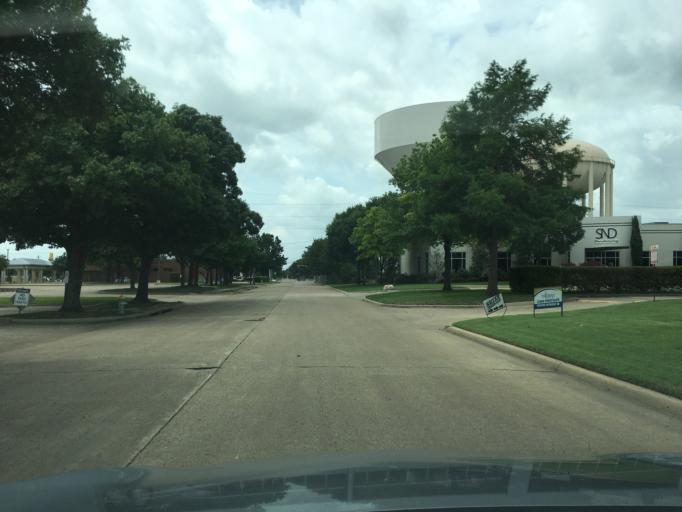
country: US
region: Texas
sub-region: Dallas County
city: Richardson
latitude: 32.9111
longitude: -96.7025
